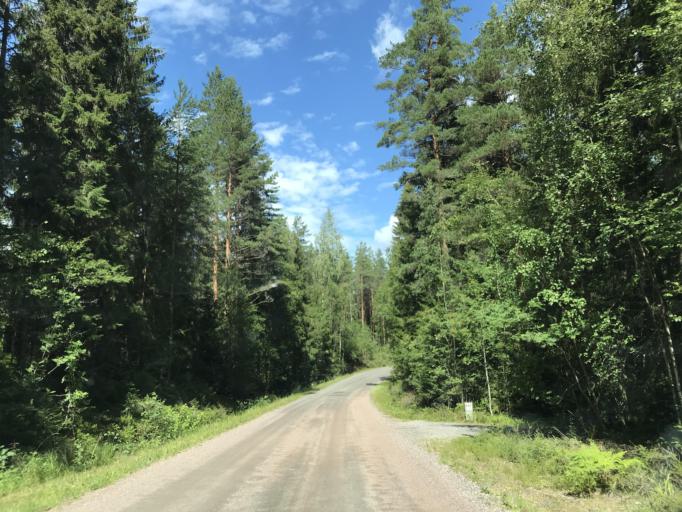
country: FI
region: Uusimaa
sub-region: Helsinki
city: Kaerkoelae
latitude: 60.6256
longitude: 23.7720
